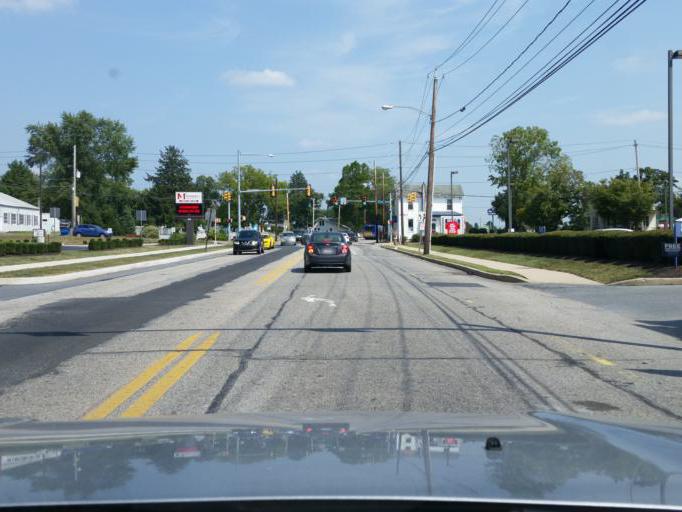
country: US
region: Pennsylvania
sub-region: Dauphin County
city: Middletown
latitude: 40.2013
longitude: -76.7253
